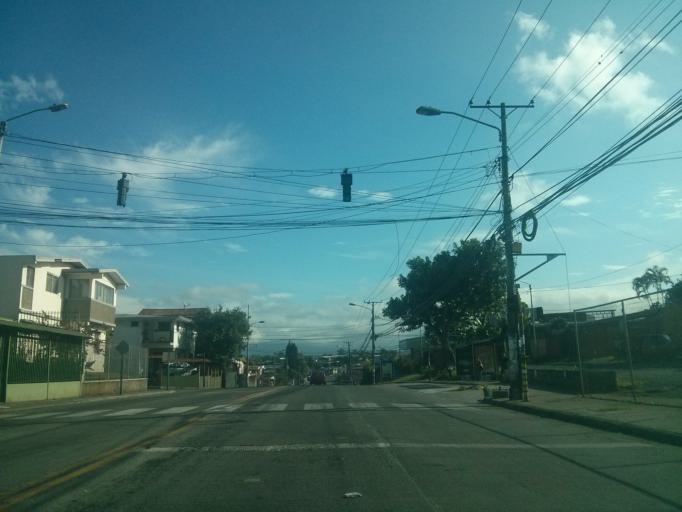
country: CR
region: San Jose
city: San Pedro
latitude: 9.9112
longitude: -84.0573
